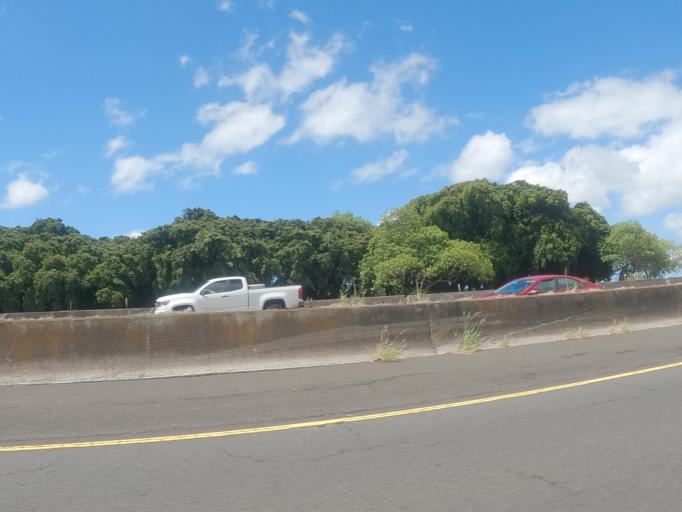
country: US
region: Hawaii
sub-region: Honolulu County
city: Halawa
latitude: 21.3723
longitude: -157.9233
